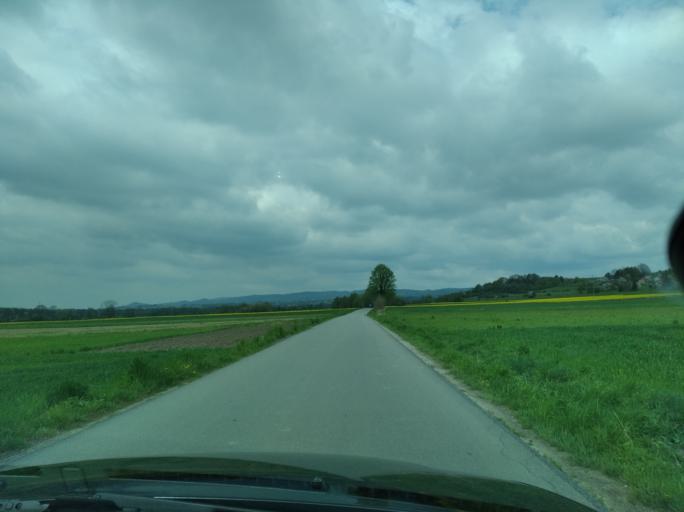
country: PL
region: Subcarpathian Voivodeship
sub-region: Powiat brzozowski
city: Jablonica Polska
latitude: 49.6815
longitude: 21.8987
